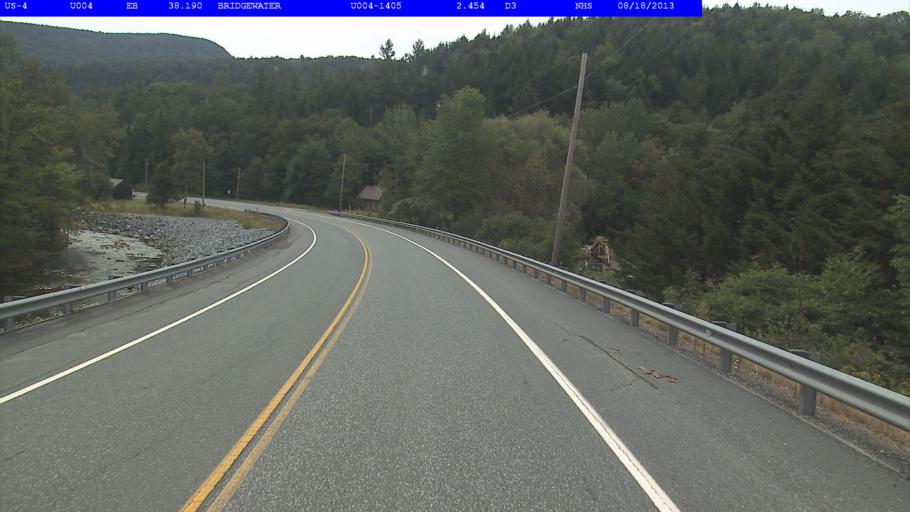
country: US
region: Vermont
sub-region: Windsor County
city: Woodstock
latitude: 43.5951
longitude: -72.7093
